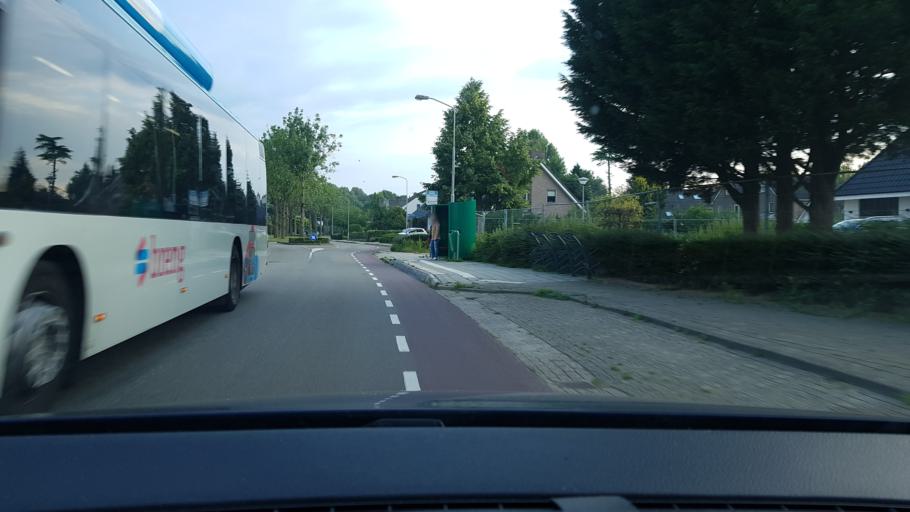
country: NL
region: Gelderland
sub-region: Gemeente Beuningen
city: Beuningen
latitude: 51.8597
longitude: 5.7814
